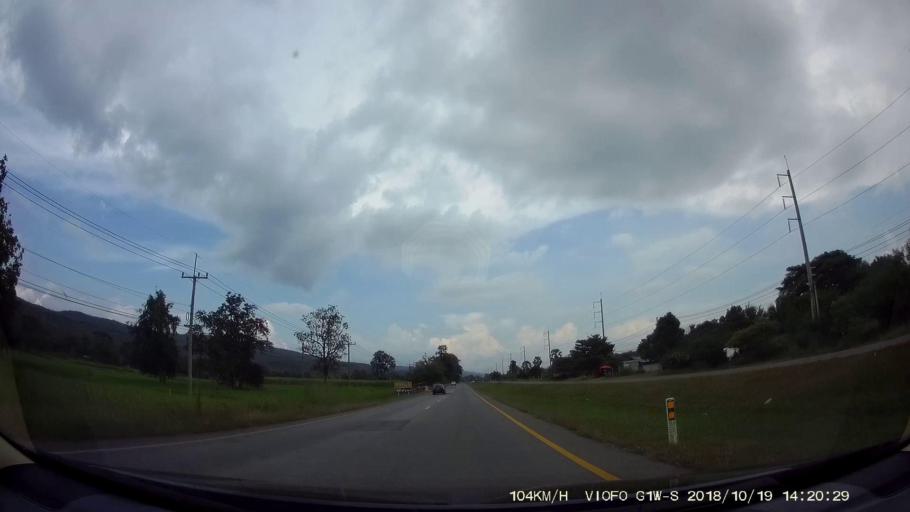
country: TH
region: Chaiyaphum
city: Kaeng Khro
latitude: 16.0409
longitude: 102.2563
